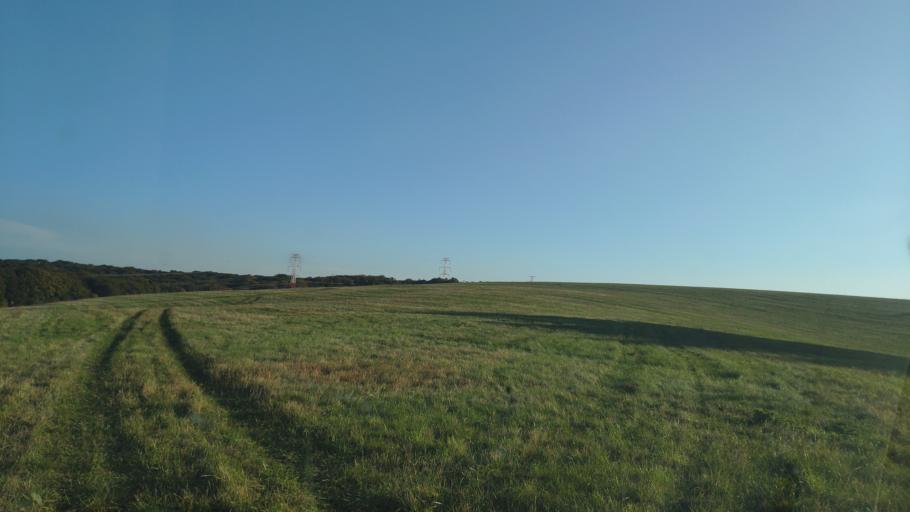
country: SK
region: Kosicky
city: Kosice
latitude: 48.7161
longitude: 21.1674
